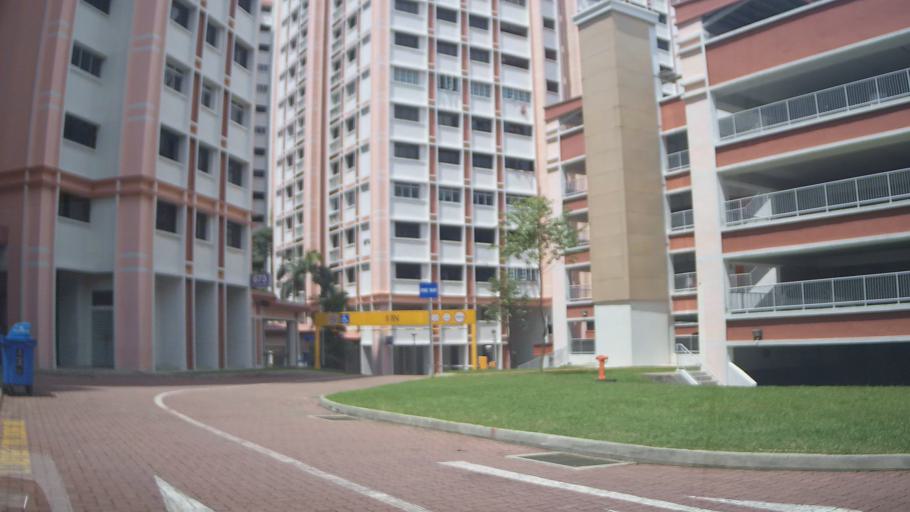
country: MY
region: Johor
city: Johor Bahru
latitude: 1.4015
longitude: 103.7483
